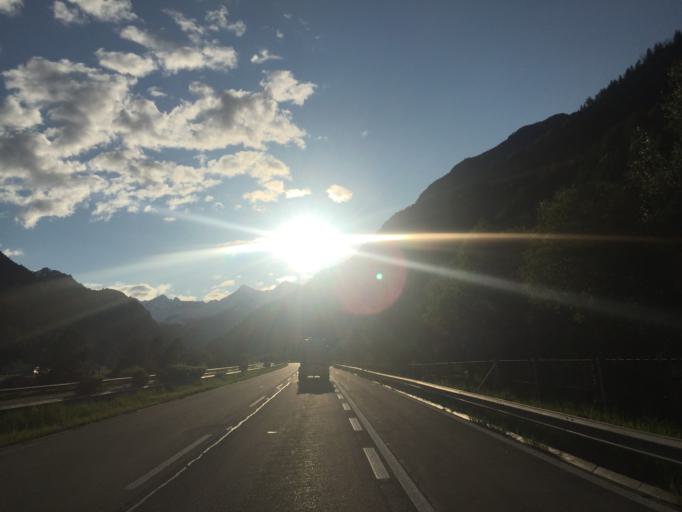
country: CH
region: Ticino
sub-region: Leventina District
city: Airolo
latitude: 46.5138
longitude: 8.6966
